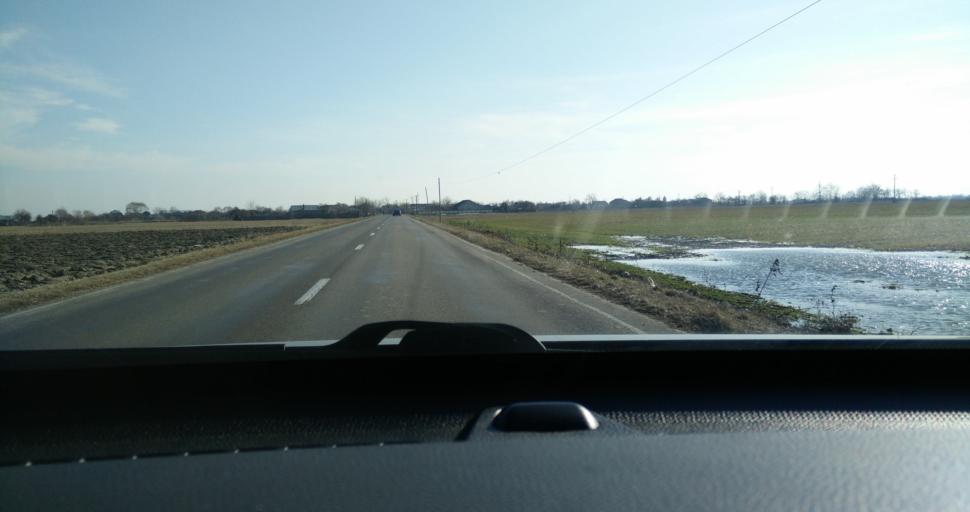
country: RO
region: Vrancea
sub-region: Comuna Nanesti
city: Nanesti
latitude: 45.5580
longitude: 27.4999
